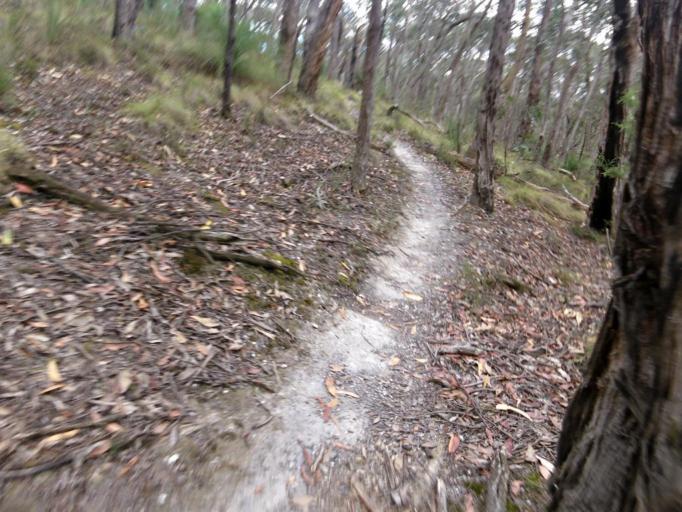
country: AU
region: Victoria
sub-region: Melton
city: Melton West
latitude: -37.4888
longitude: 144.5414
